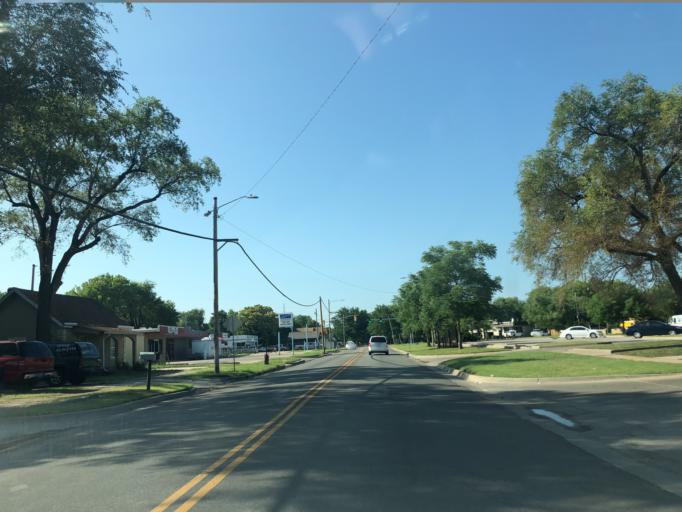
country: US
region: Kansas
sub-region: Sedgwick County
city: Wichita
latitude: 37.7311
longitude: -97.3448
